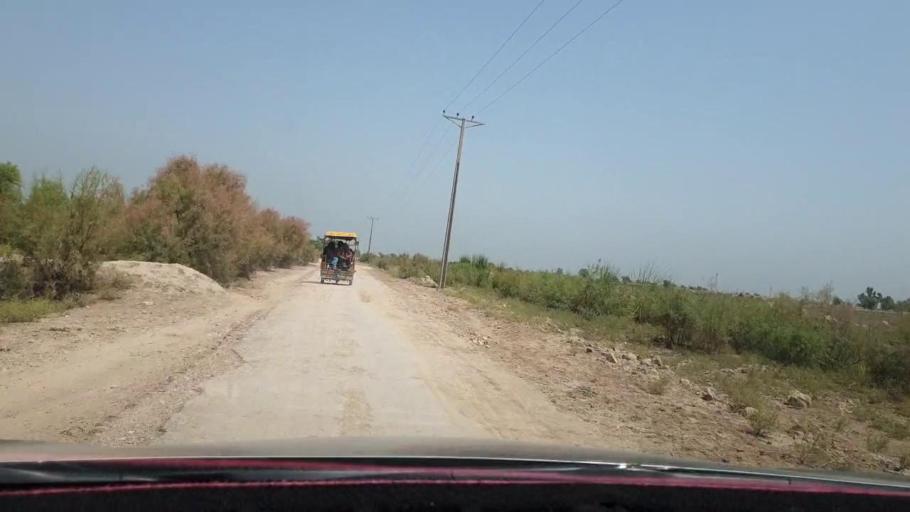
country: PK
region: Sindh
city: Warah
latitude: 27.4339
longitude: 67.7150
